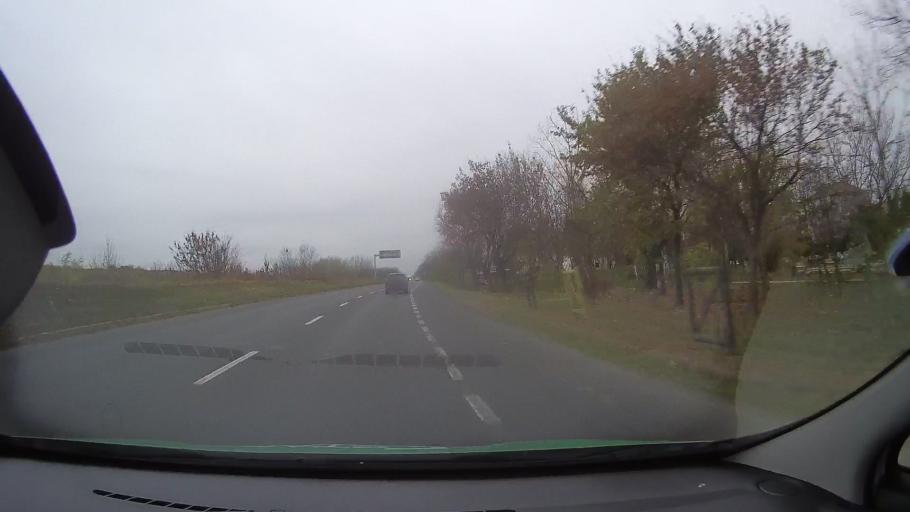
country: RO
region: Ialomita
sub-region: Comuna Slobozia
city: Slobozia
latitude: 44.5625
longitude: 27.3794
